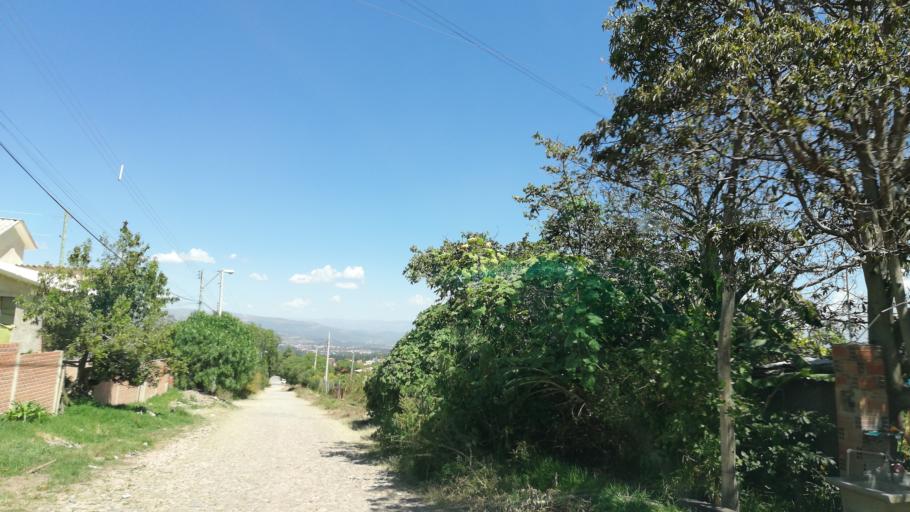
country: BO
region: Cochabamba
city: Cochabamba
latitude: -17.3266
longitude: -66.2140
